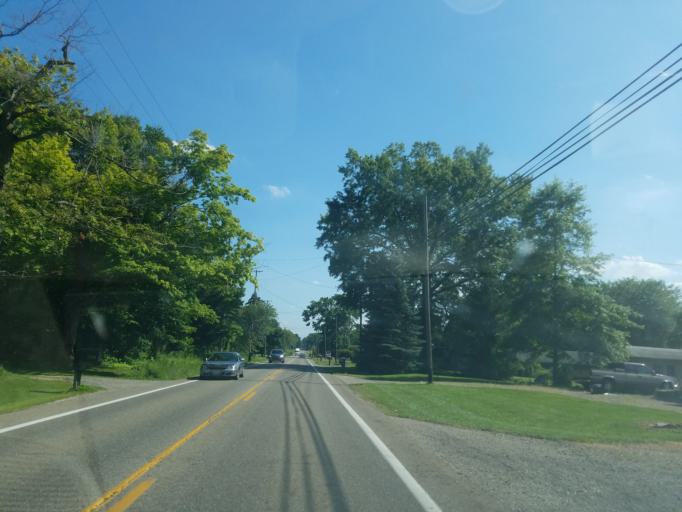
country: US
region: Ohio
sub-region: Portage County
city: Ravenna
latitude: 41.1998
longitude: -81.2461
